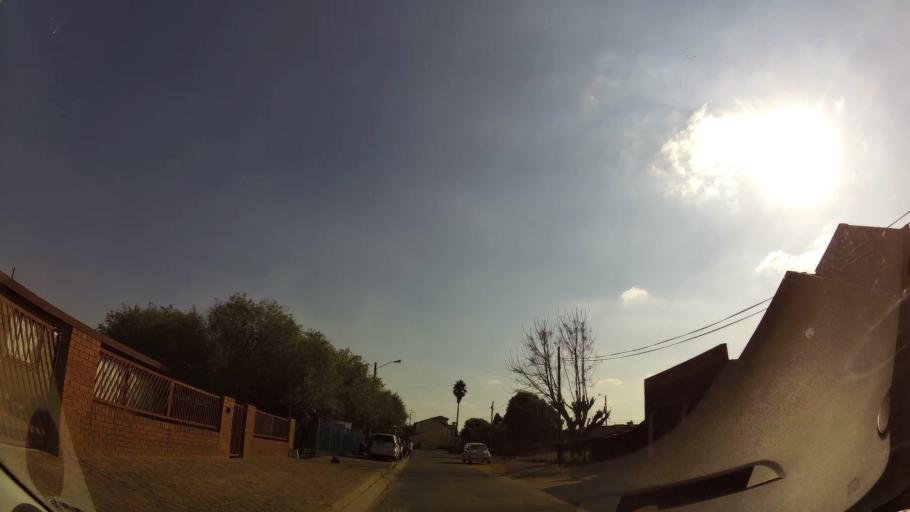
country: ZA
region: Gauteng
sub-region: Ekurhuleni Metropolitan Municipality
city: Brakpan
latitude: -26.1598
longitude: 28.4002
